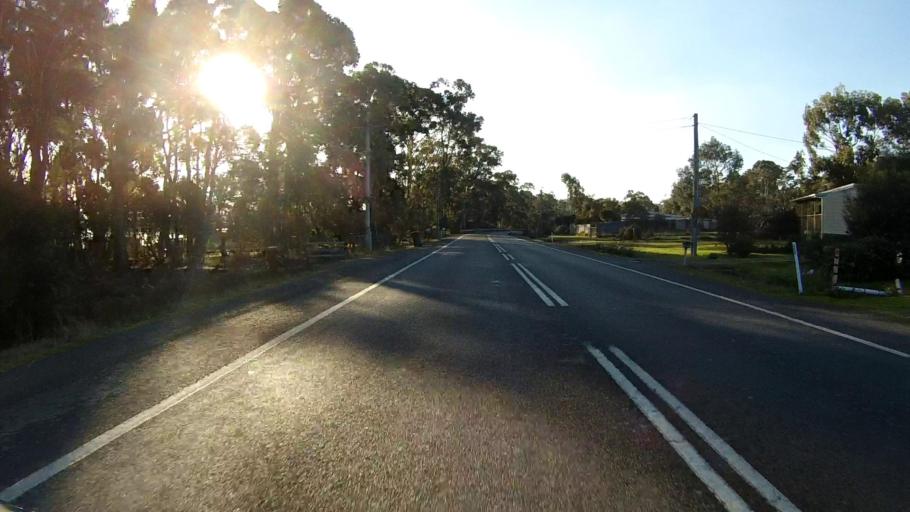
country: AU
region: Tasmania
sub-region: Clarence
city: Sandford
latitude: -43.0373
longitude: 147.8648
